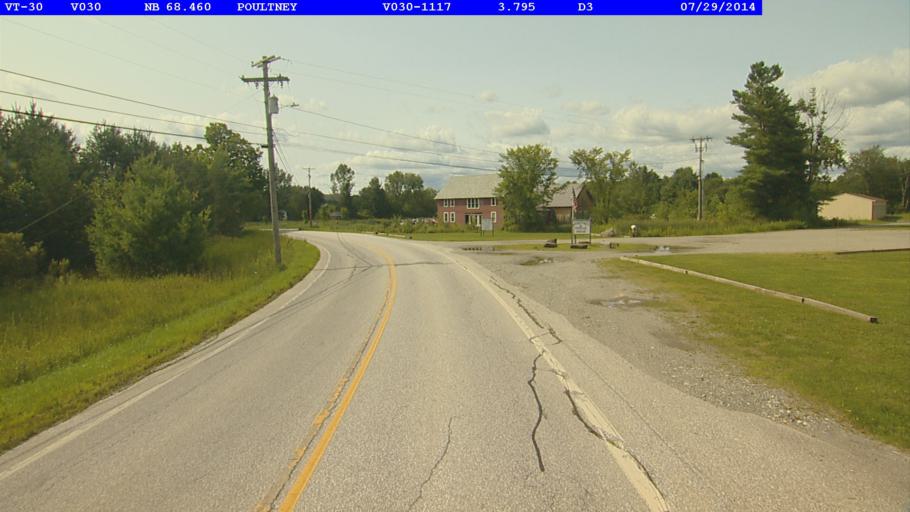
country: US
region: Vermont
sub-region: Rutland County
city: Poultney
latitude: 43.5122
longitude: -73.2214
